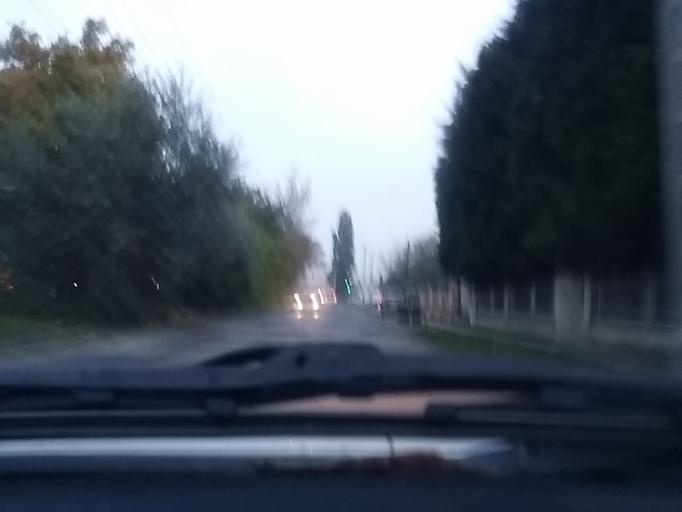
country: HU
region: Budapest
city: Budapest XVI. keruelet
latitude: 47.5174
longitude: 19.1412
